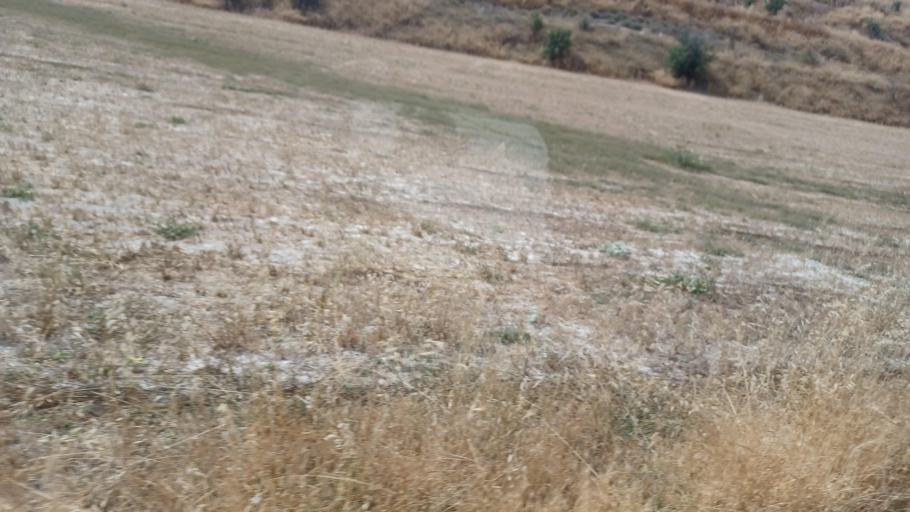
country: CY
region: Larnaka
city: Dhromolaxia
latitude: 34.9145
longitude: 33.5442
